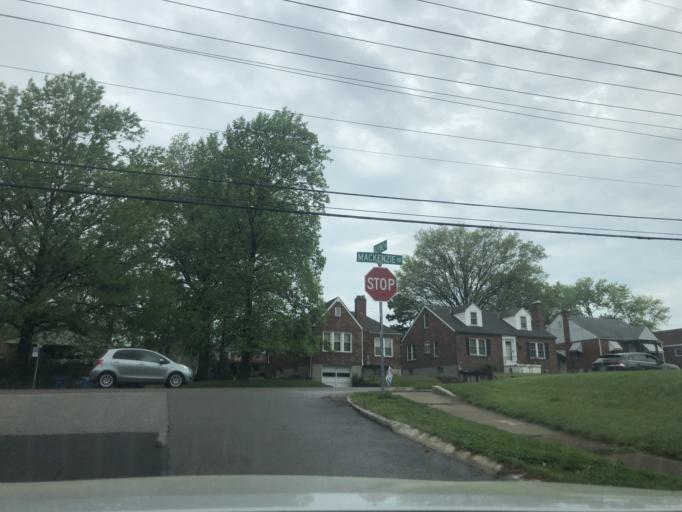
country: US
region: Missouri
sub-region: Saint Louis County
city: Affton
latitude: 38.5484
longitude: -90.3223
